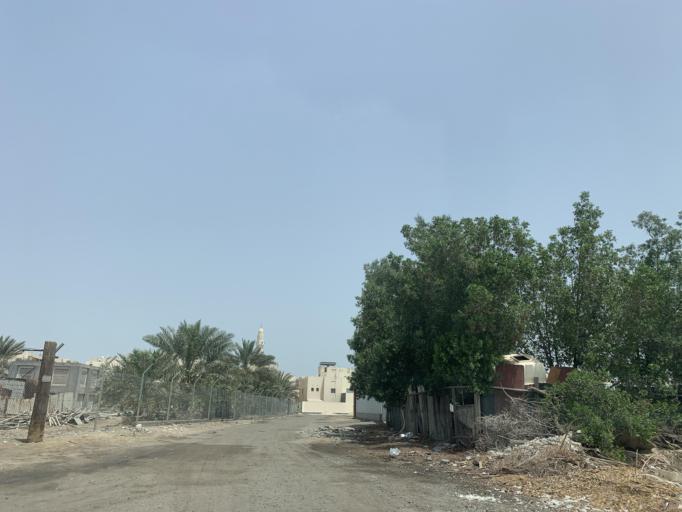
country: BH
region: Northern
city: Sitrah
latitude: 26.1380
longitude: 50.5934
